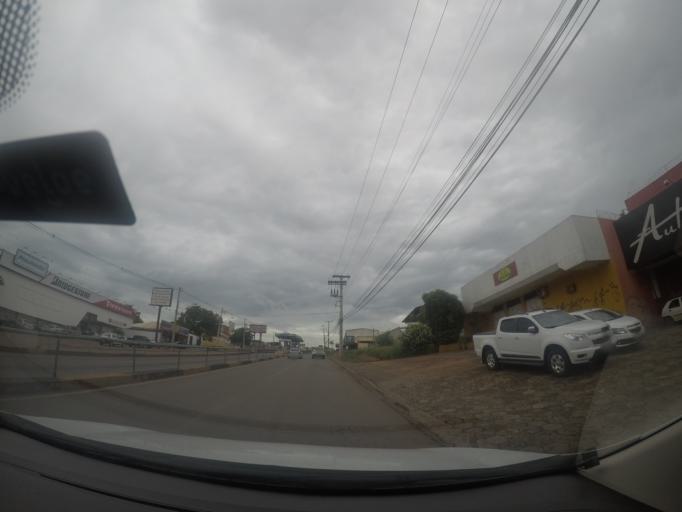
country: BR
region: Goias
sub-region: Goiania
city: Goiania
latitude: -16.6645
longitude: -49.3190
